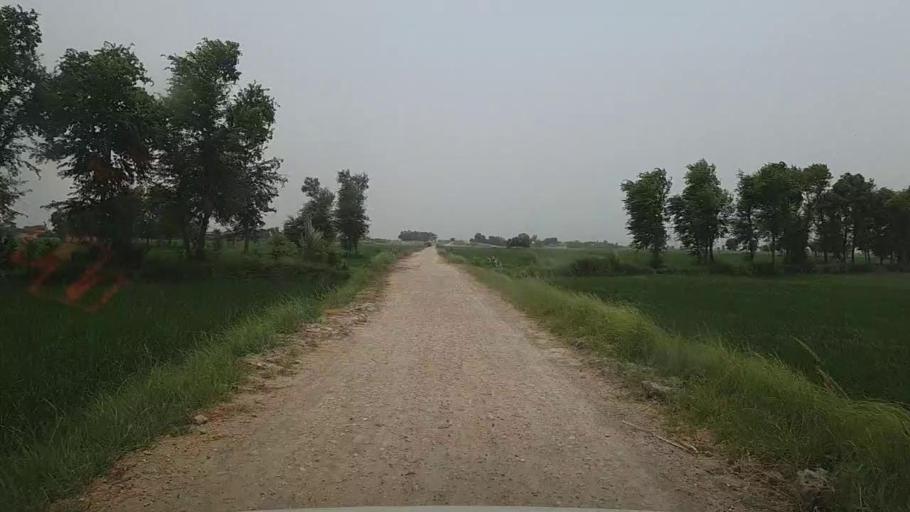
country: PK
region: Sindh
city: Sita Road
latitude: 27.0567
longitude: 67.8524
